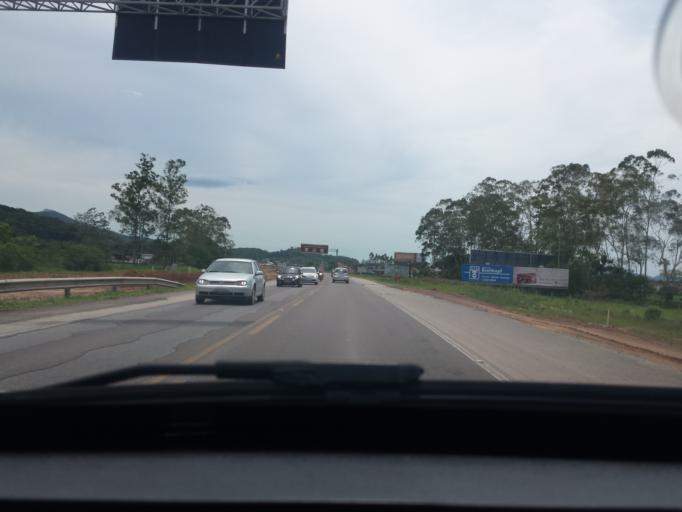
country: BR
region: Santa Catarina
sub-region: Gaspar
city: Gaspar
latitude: -26.9121
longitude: -48.9538
